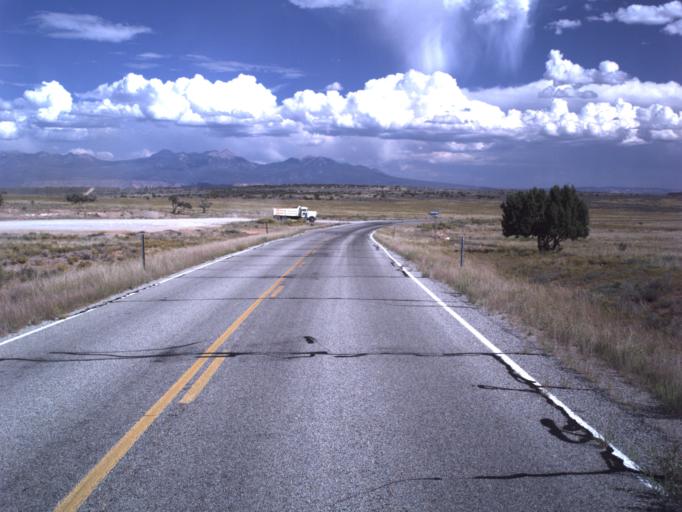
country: US
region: Utah
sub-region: Grand County
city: Moab
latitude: 38.5444
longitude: -109.7627
